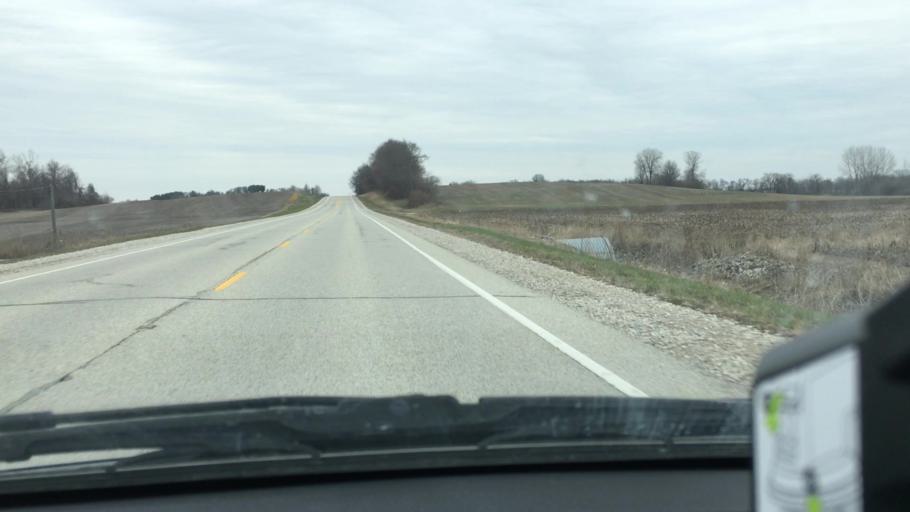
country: US
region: Indiana
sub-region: Greene County
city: Bloomfield
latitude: 38.9517
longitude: -87.0167
